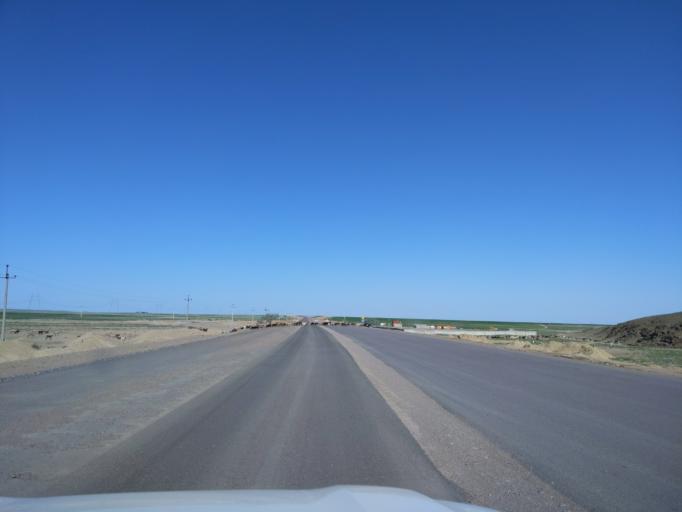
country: KZ
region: Almaty Oblysy
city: Bakanas
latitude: 44.0943
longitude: 75.9868
